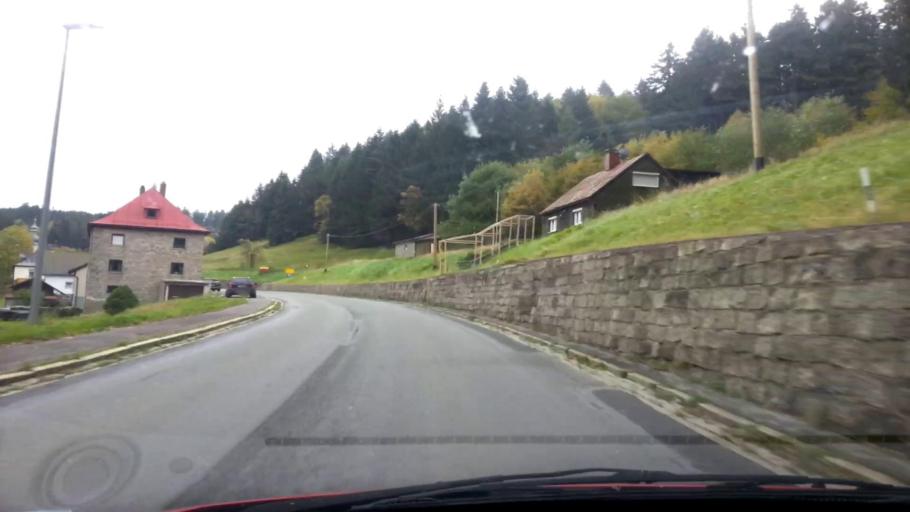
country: DE
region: Bavaria
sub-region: Upper Franconia
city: Warmensteinach
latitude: 50.0008
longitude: 11.7946
